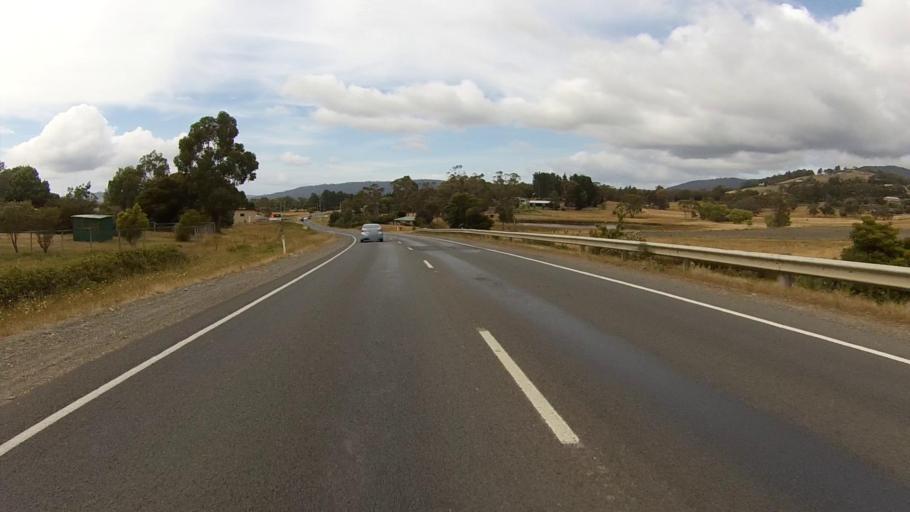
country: AU
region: Tasmania
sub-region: Kingborough
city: Margate
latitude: -43.0310
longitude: 147.2646
